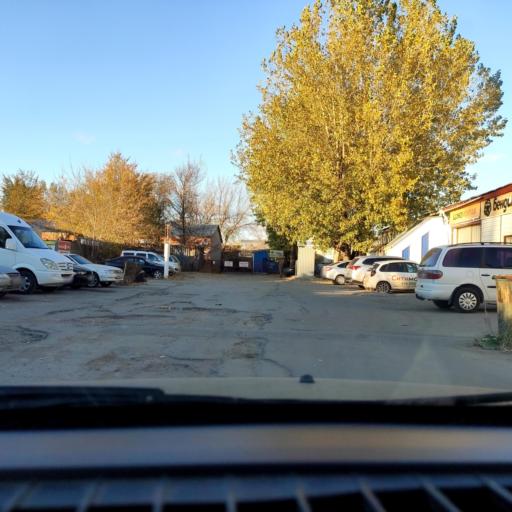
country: RU
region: Samara
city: Tol'yatti
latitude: 53.5317
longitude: 49.2601
